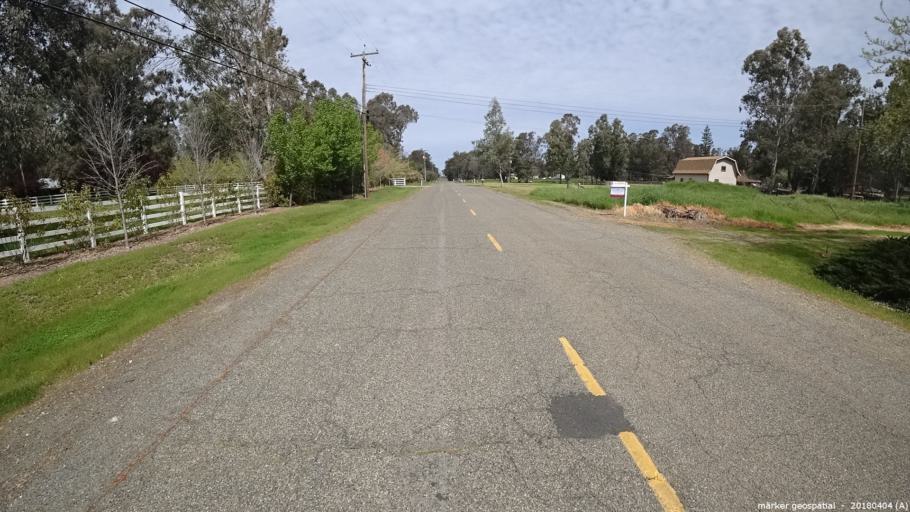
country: US
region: California
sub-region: Sacramento County
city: Clay
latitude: 38.3250
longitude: -121.1452
